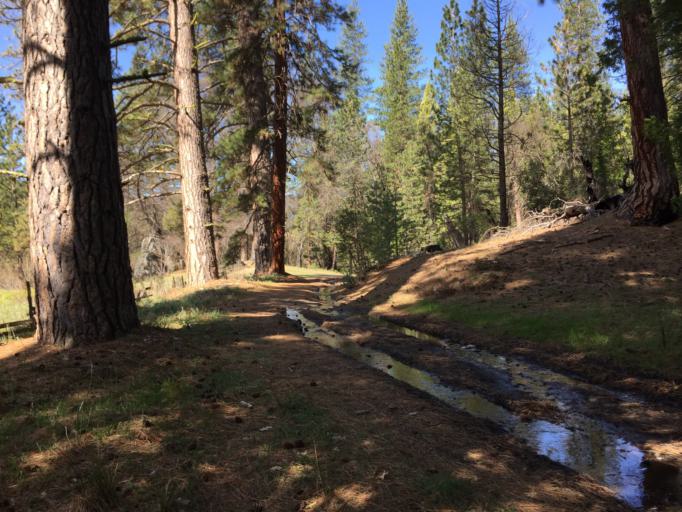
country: US
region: California
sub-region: Madera County
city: Ahwahnee
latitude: 37.5310
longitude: -119.6413
